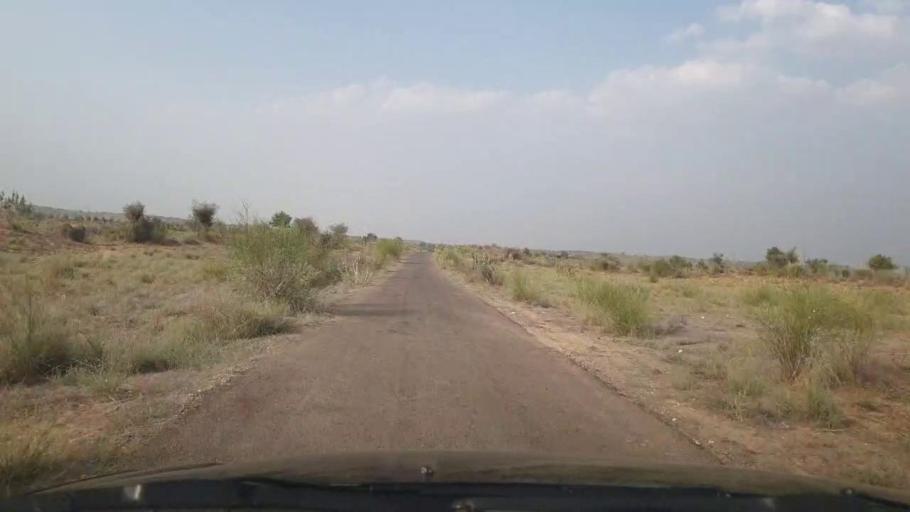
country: PK
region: Sindh
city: Islamkot
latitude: 25.0582
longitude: 70.5607
